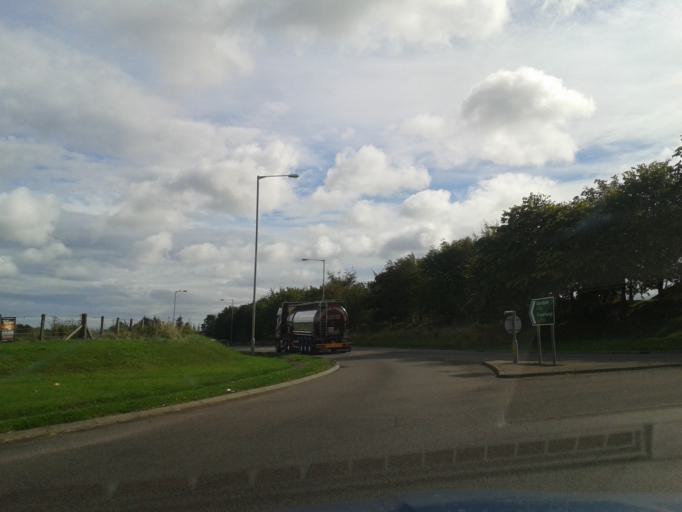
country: GB
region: Scotland
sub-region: Moray
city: Forres
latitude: 57.6161
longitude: -3.5953
